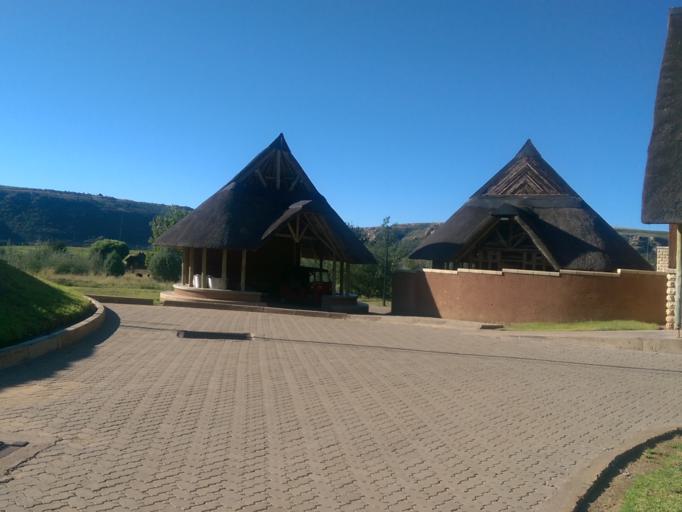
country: LS
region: Maseru
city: Maseru
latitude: -29.3454
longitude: 27.6619
